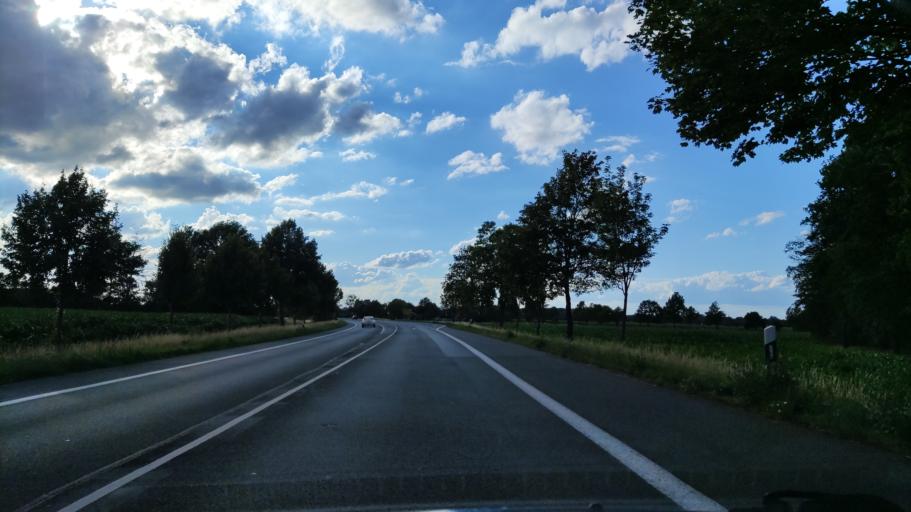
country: DE
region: North Rhine-Westphalia
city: Ahlen
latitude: 51.7753
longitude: 7.8465
